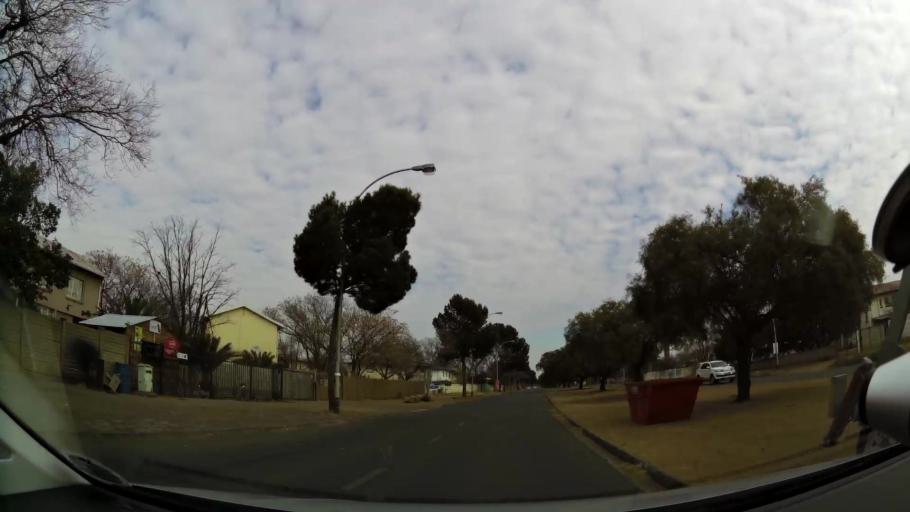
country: ZA
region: Orange Free State
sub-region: Mangaung Metropolitan Municipality
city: Bloemfontein
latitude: -29.1312
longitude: 26.1894
